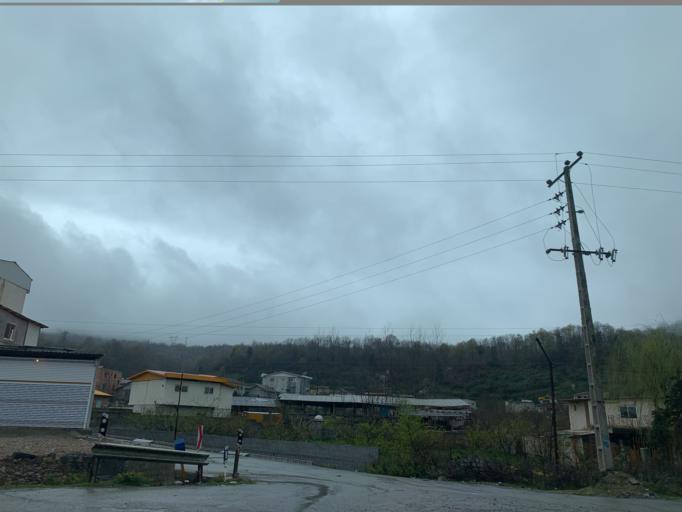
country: IR
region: Mazandaran
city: Amol
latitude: 36.3650
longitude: 52.3573
